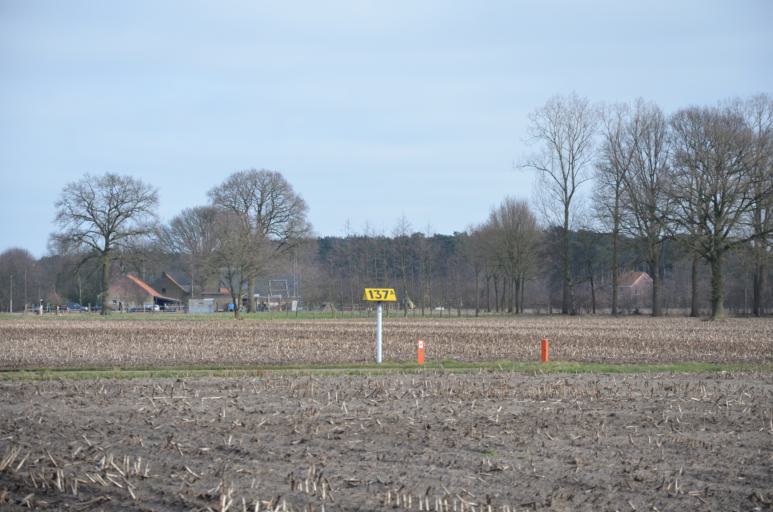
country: BE
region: Flanders
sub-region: Provincie Antwerpen
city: Herentals
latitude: 51.2099
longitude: 4.8461
